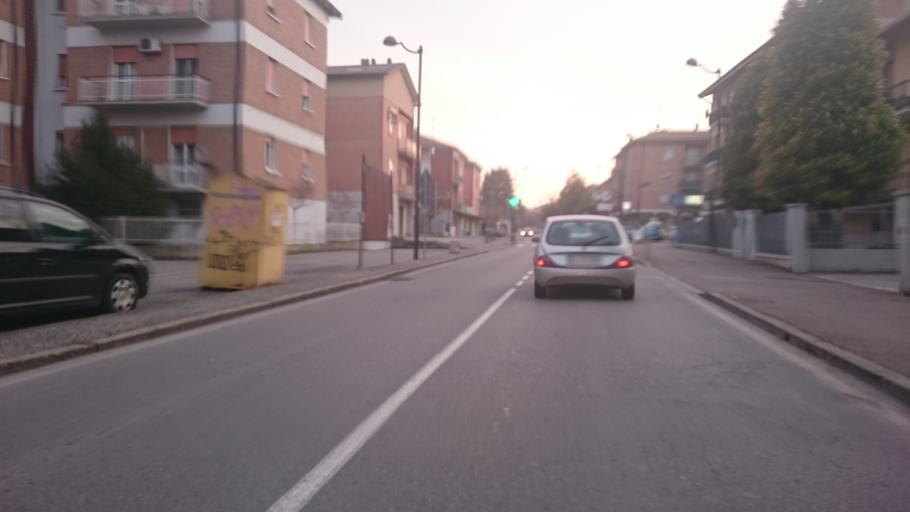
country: IT
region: Emilia-Romagna
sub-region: Provincia di Reggio Emilia
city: Reggio nell'Emilia
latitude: 44.7135
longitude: 10.6330
